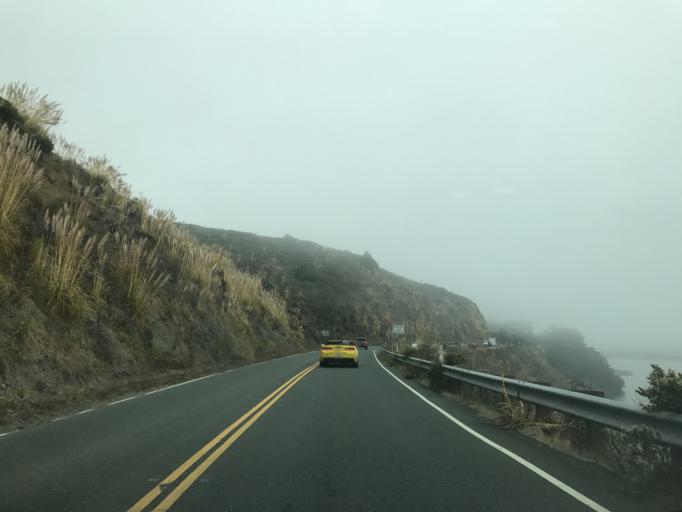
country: US
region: California
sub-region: Sonoma County
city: Monte Rio
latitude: 38.4533
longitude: -123.1304
